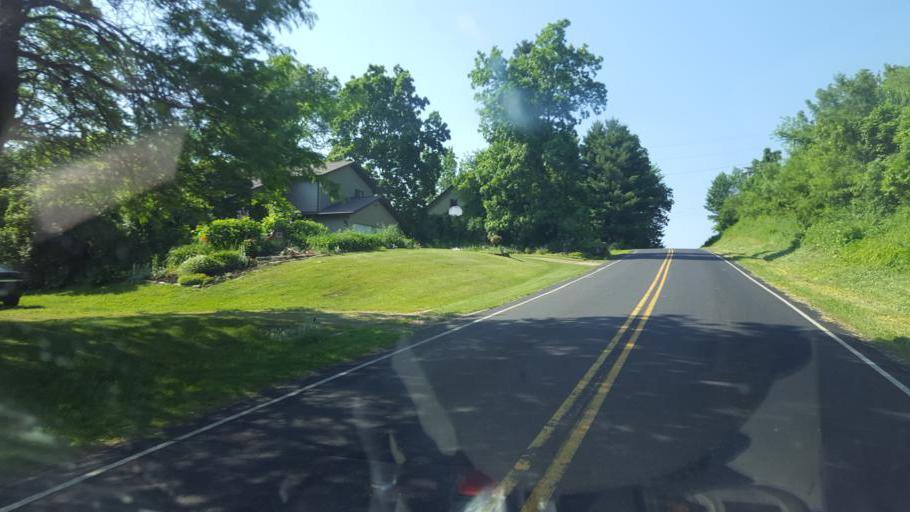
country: US
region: Wisconsin
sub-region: Vernon County
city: Hillsboro
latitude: 43.6611
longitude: -90.3460
